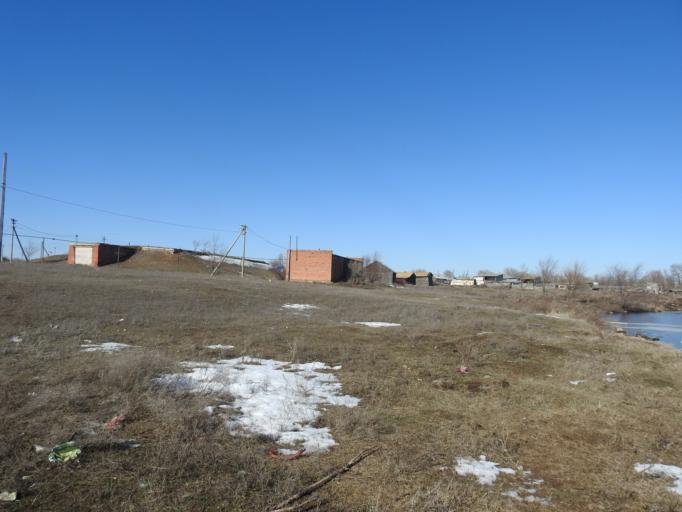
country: RU
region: Saratov
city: Yershov
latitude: 51.3702
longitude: 48.2359
